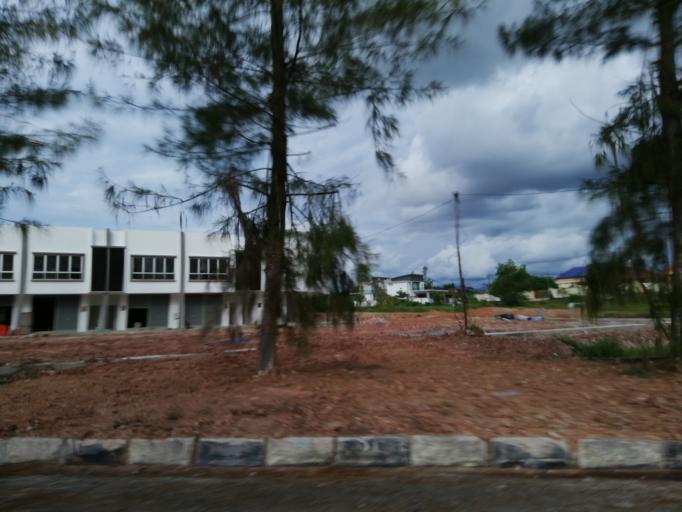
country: MY
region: Penang
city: Tasek Glugor
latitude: 5.5054
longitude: 100.6249
